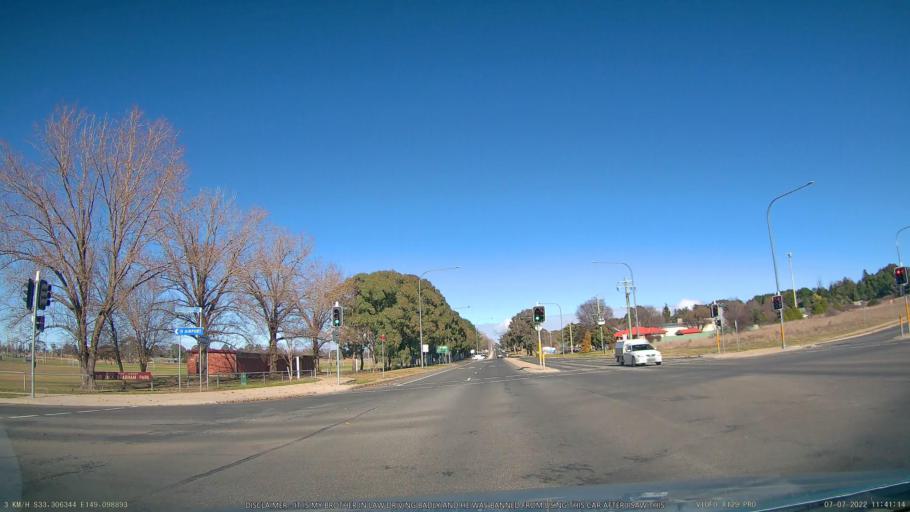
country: AU
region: New South Wales
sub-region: Orange Municipality
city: Orange
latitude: -33.3065
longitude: 149.0988
